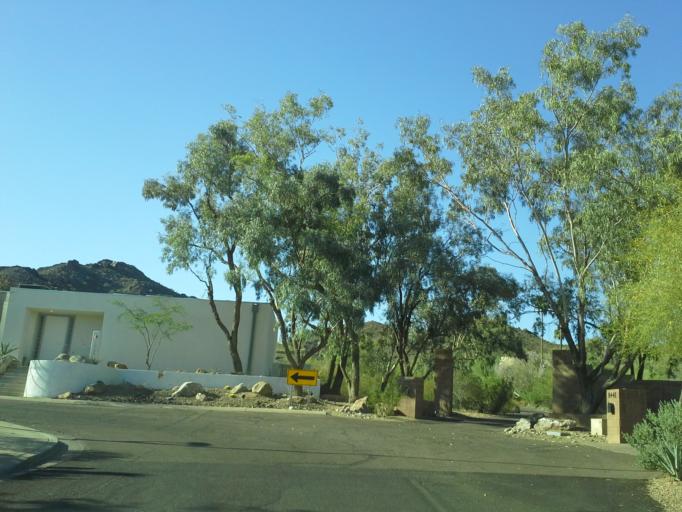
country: US
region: Arizona
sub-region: Maricopa County
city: Paradise Valley
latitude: 33.5604
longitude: -112.0438
